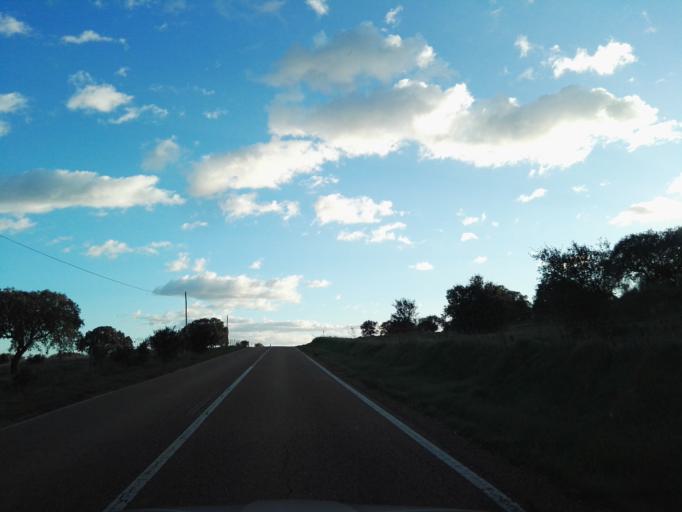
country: PT
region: Portalegre
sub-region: Elvas
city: Elvas
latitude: 38.8150
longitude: -7.1670
